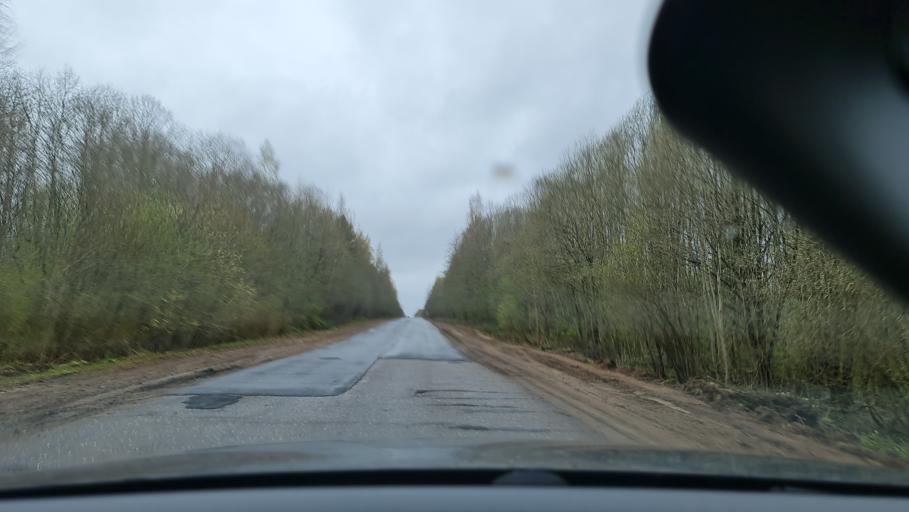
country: RU
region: Novgorod
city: Demyansk
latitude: 57.7409
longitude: 32.5730
